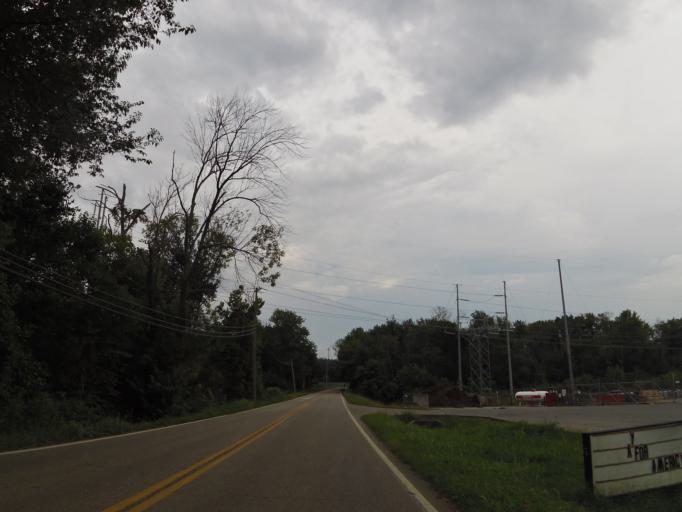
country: US
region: Tennessee
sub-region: Loudon County
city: Greenback
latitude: 35.6546
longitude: -84.1552
